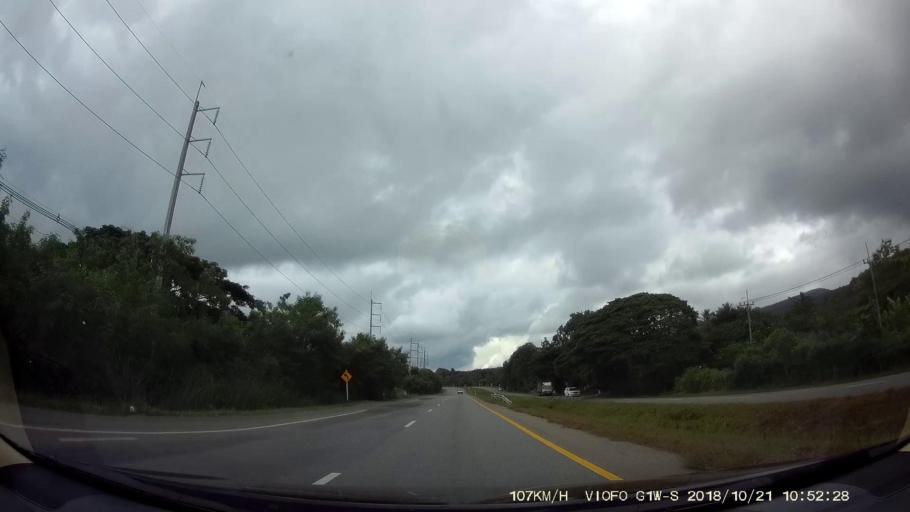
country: TH
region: Chaiyaphum
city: Khon Sawan
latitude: 15.9759
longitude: 102.1927
